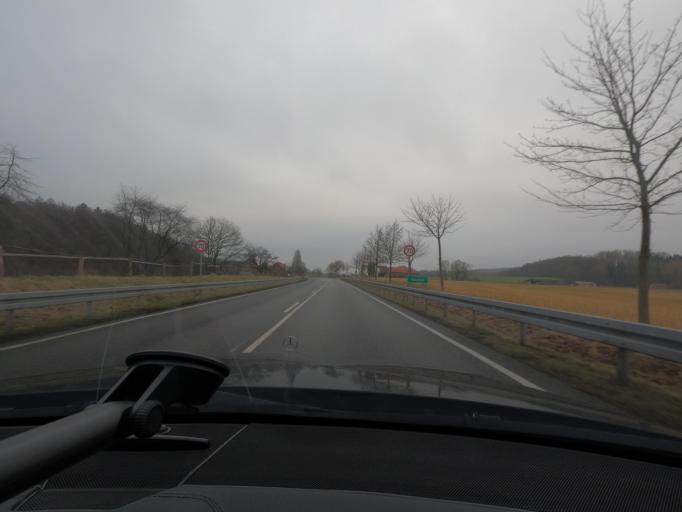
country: DE
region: Hesse
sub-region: Regierungsbezirk Kassel
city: Bad Arolsen
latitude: 51.4503
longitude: 9.0142
